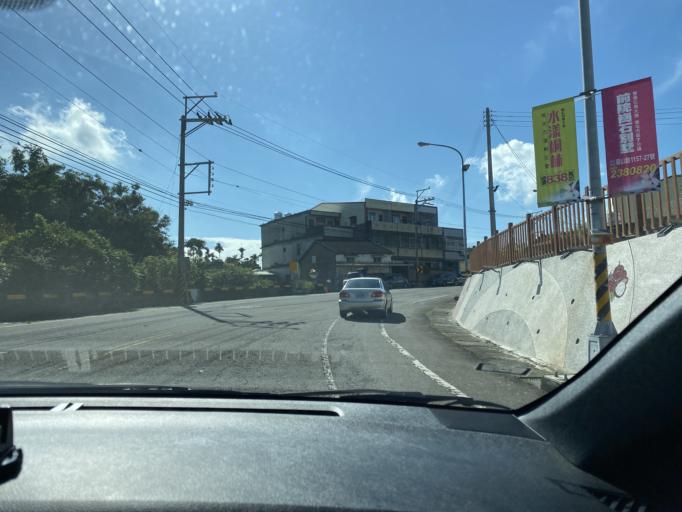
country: TW
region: Taiwan
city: Zhongxing New Village
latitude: 23.9738
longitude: 120.6222
